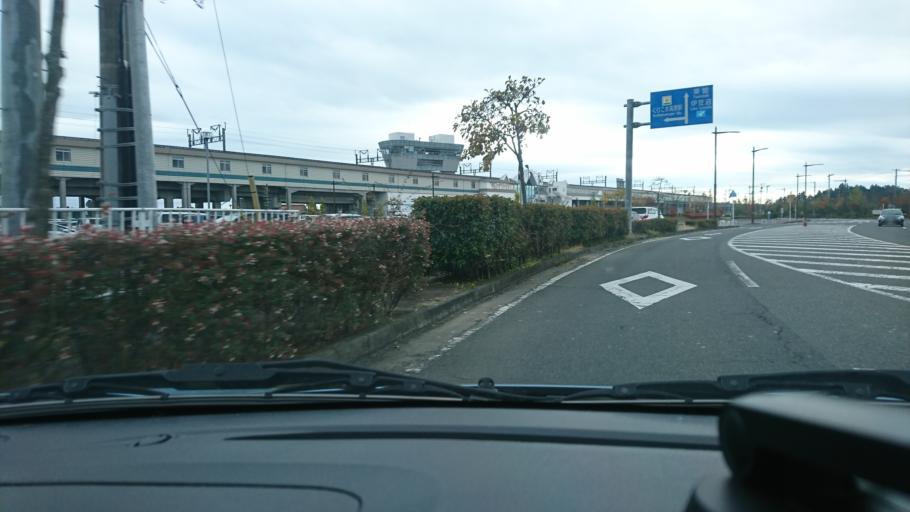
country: JP
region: Iwate
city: Ichinoseki
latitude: 38.7507
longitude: 141.0715
